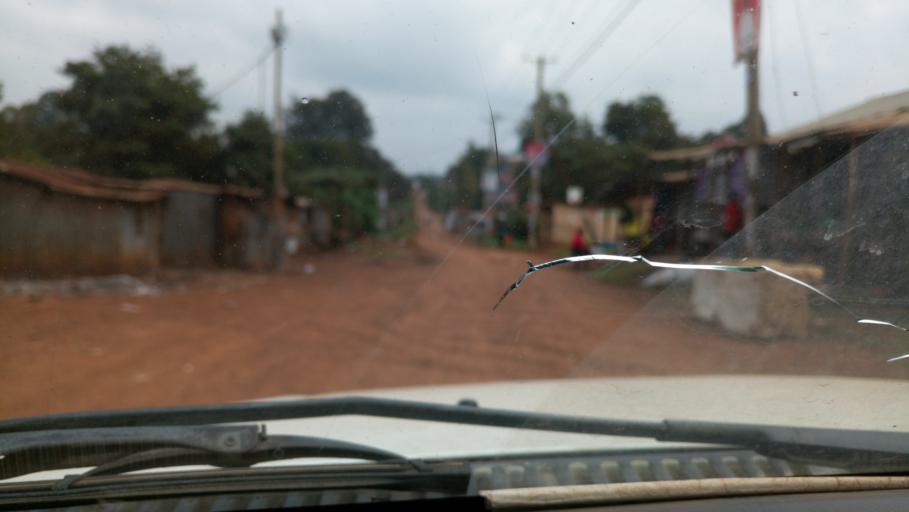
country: KE
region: Kiambu
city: Kikuyu
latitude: -1.2791
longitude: 36.7222
